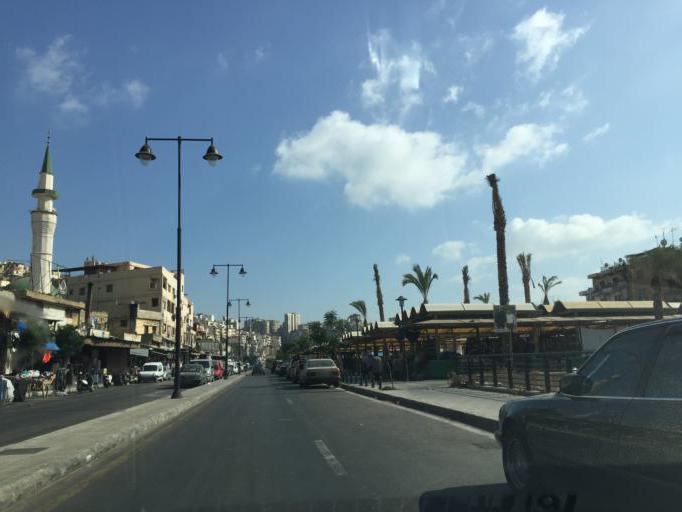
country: LB
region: Liban-Nord
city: Tripoli
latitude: 34.4399
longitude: 35.8475
